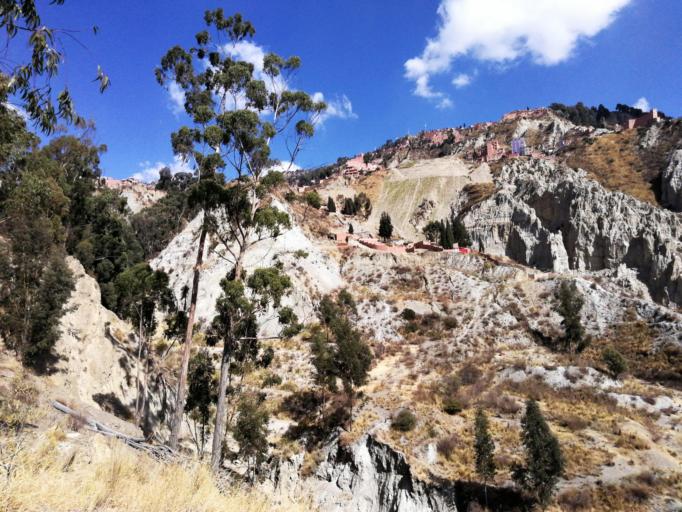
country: BO
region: La Paz
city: La Paz
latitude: -16.5310
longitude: -68.1331
